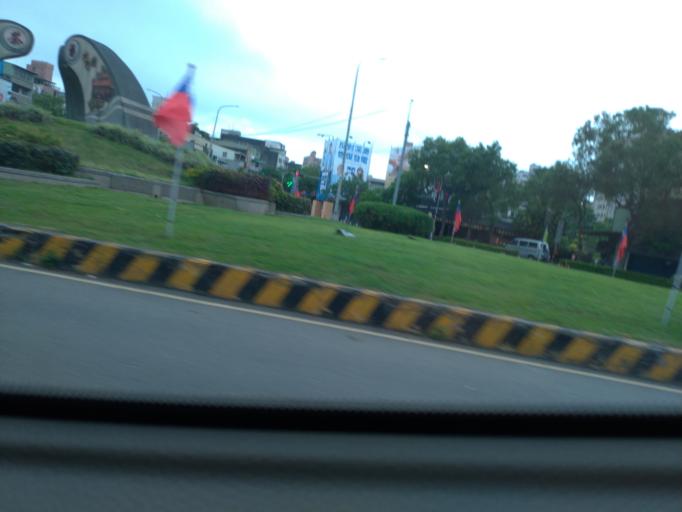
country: TW
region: Taiwan
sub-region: Taoyuan
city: Taoyuan
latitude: 24.9316
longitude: 121.3763
